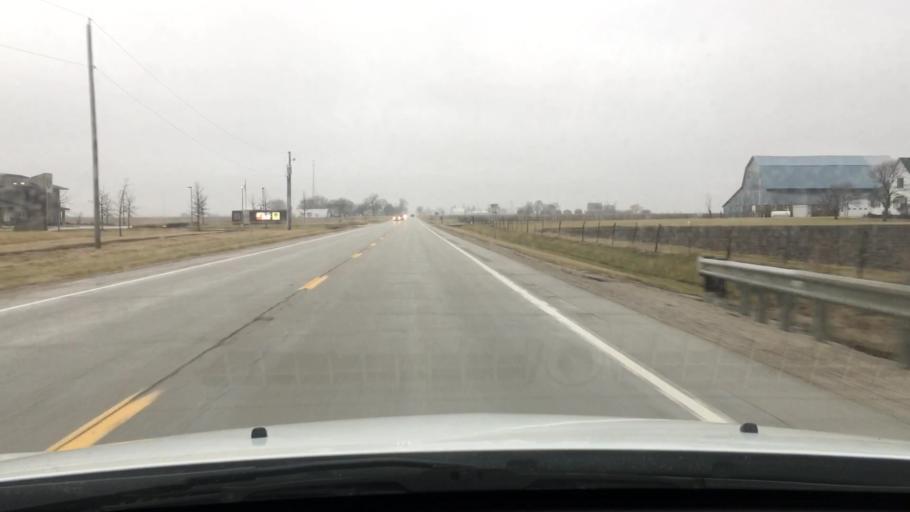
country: US
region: Illinois
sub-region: Livingston County
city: Flanagan
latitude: 40.8709
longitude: -88.8638
